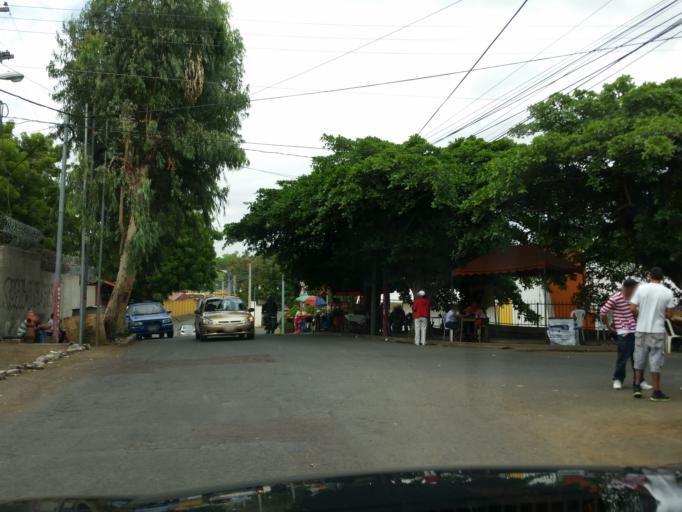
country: NI
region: Managua
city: Managua
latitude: 12.1256
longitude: -86.2669
